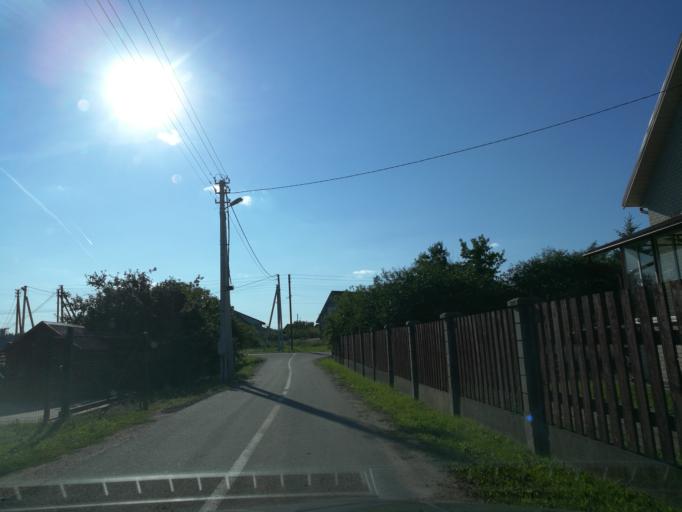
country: LT
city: Trakai
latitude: 54.6054
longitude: 24.9785
